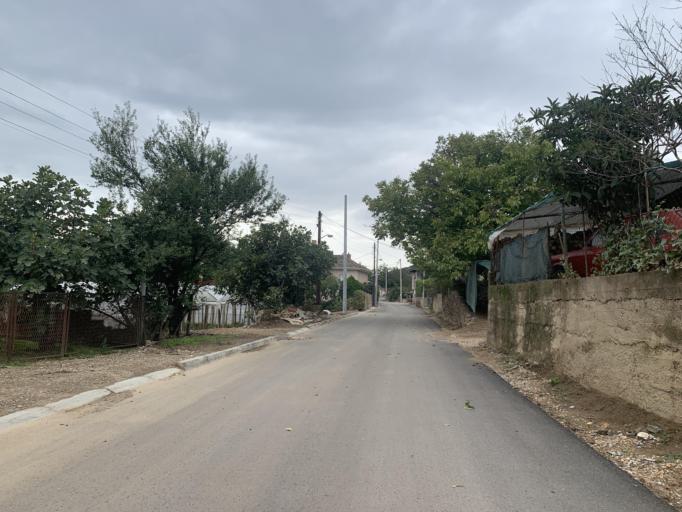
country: MK
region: Bogdanci
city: Bogdanci
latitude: 41.1915
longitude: 22.5387
